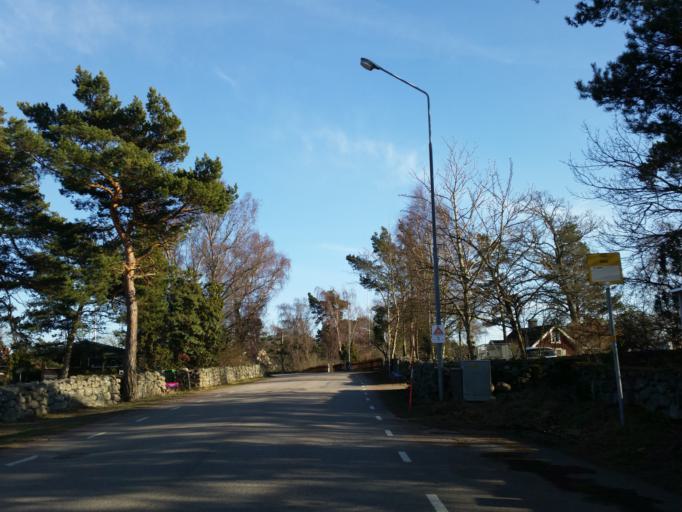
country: SE
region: Kalmar
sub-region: Kalmar Kommun
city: Lindsdal
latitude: 56.7804
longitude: 16.4109
